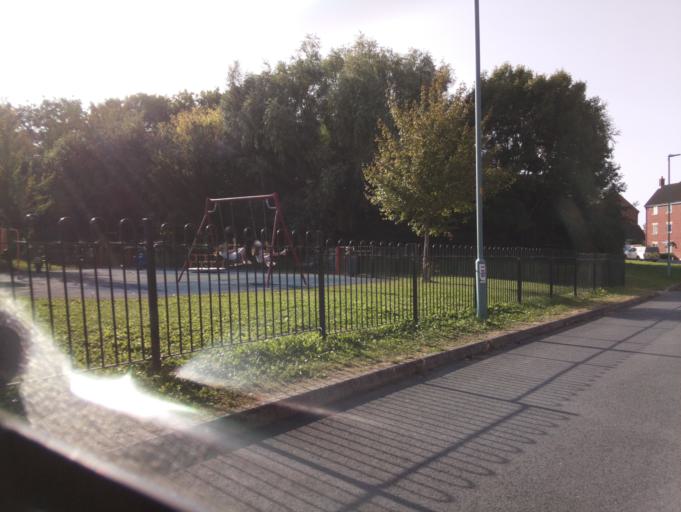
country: GB
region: England
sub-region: Gloucestershire
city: Tewkesbury
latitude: 51.9814
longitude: -2.1371
